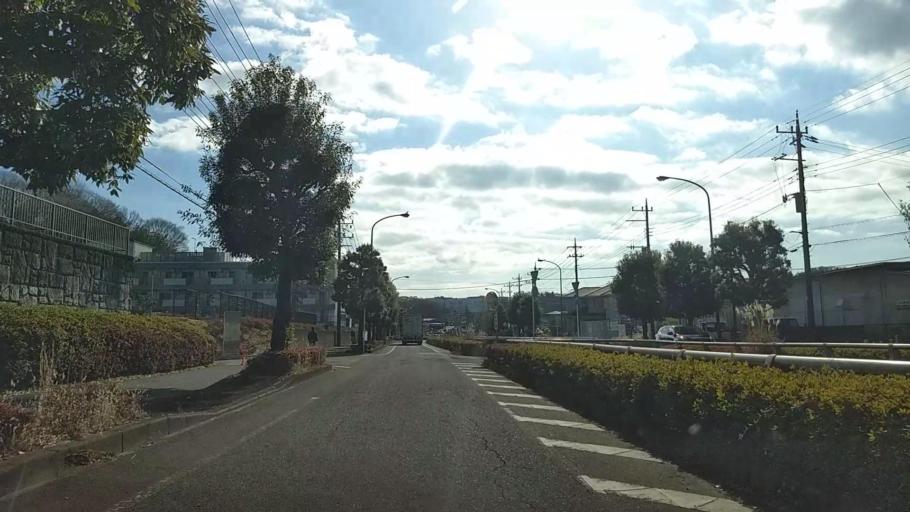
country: JP
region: Kanagawa
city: Atsugi
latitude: 35.4377
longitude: 139.3132
